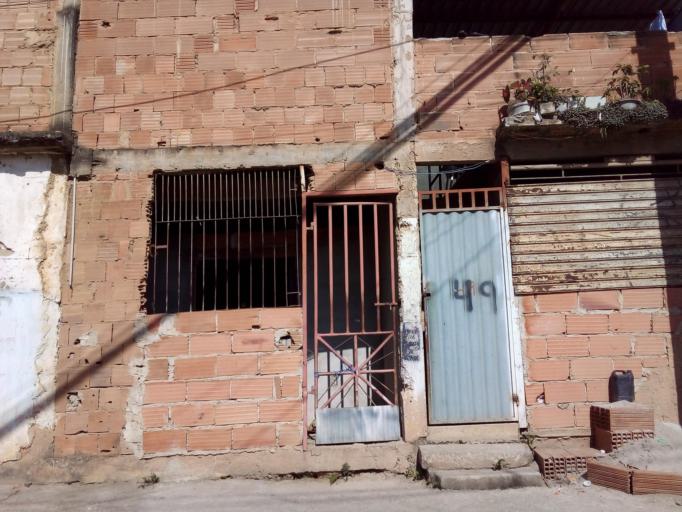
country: BR
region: Espirito Santo
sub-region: Vitoria
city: Vitoria
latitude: -20.2863
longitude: -40.3759
